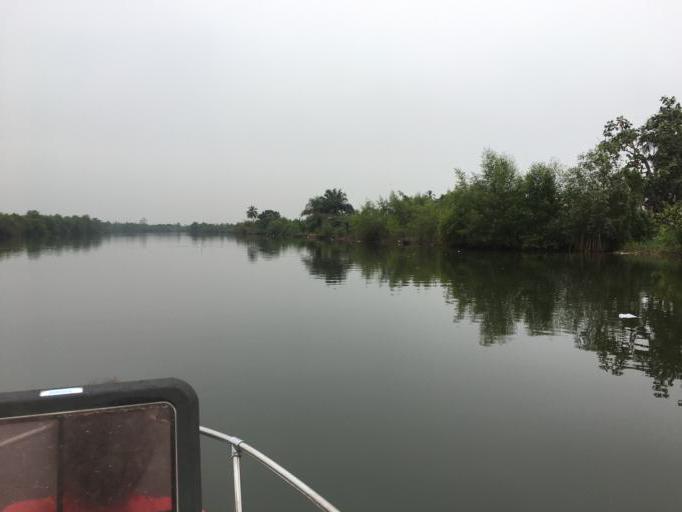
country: LR
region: Montserrado
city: Monrovia
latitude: 6.3695
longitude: -10.7774
